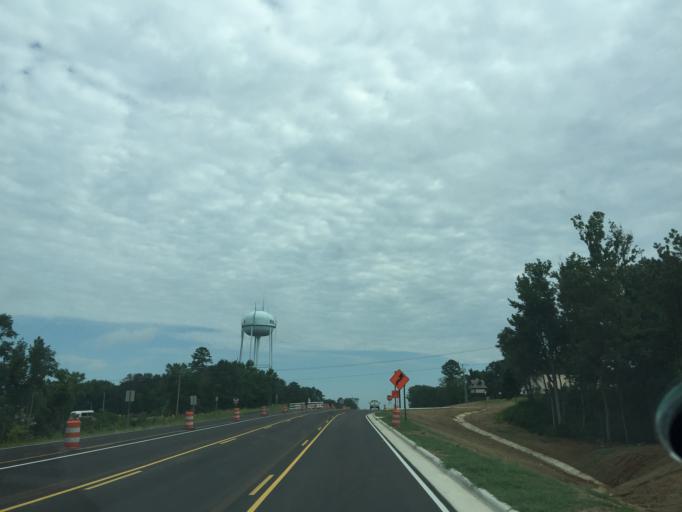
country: US
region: Mississippi
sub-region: Rankin County
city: Brandon
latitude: 32.2757
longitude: -89.9939
